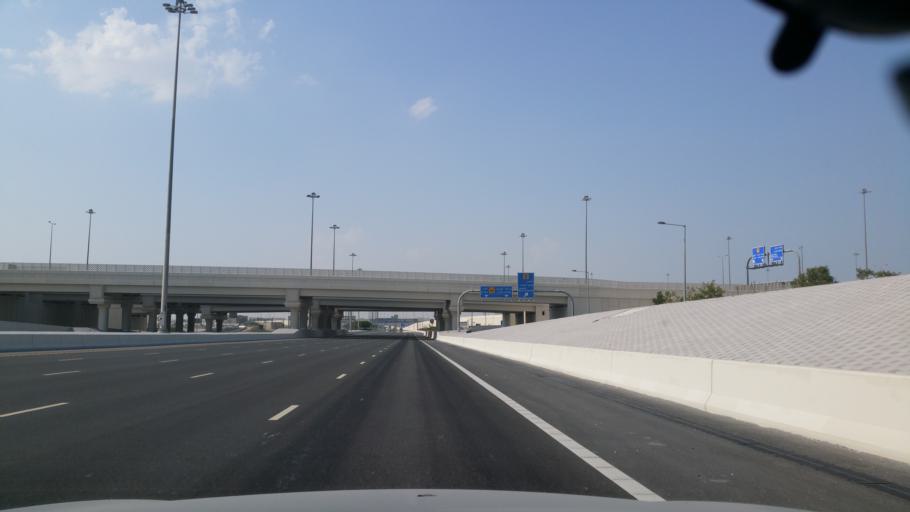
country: QA
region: Baladiyat Umm Salal
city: Umm Salal Muhammad
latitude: 25.3915
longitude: 51.4983
